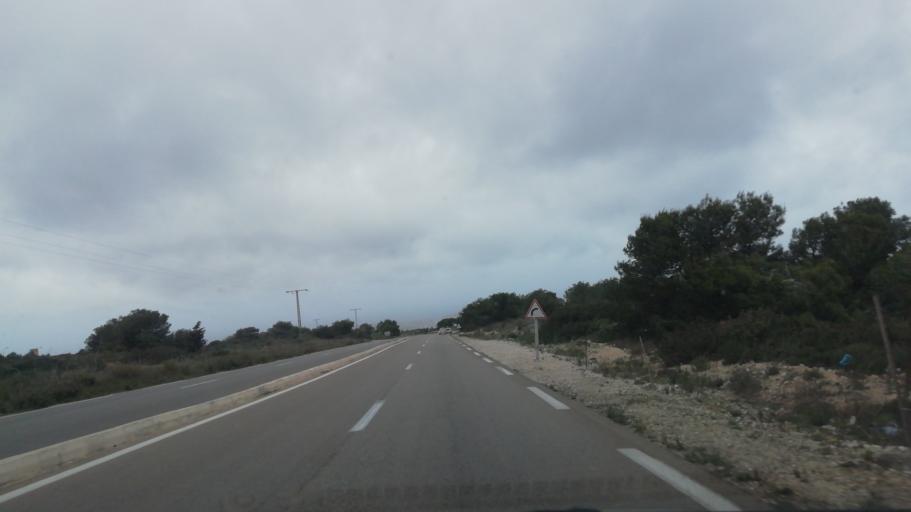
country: DZ
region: Oran
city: Mers el Kebir
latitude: 35.7169
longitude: -0.7397
